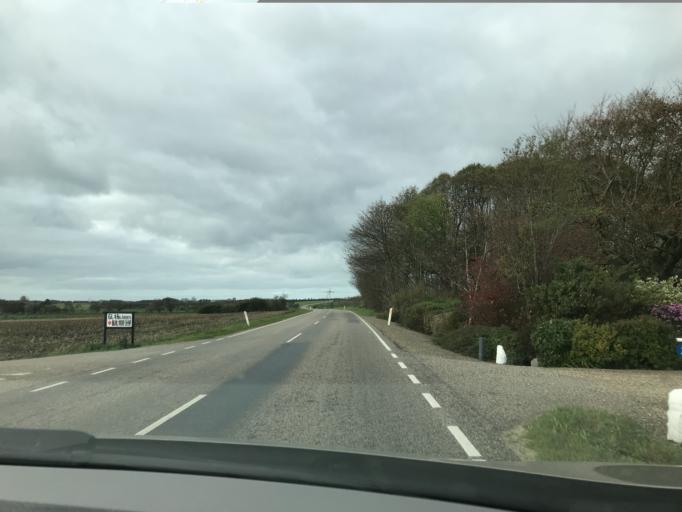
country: DK
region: South Denmark
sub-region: Varde Kommune
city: Olgod
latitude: 55.7902
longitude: 8.6851
